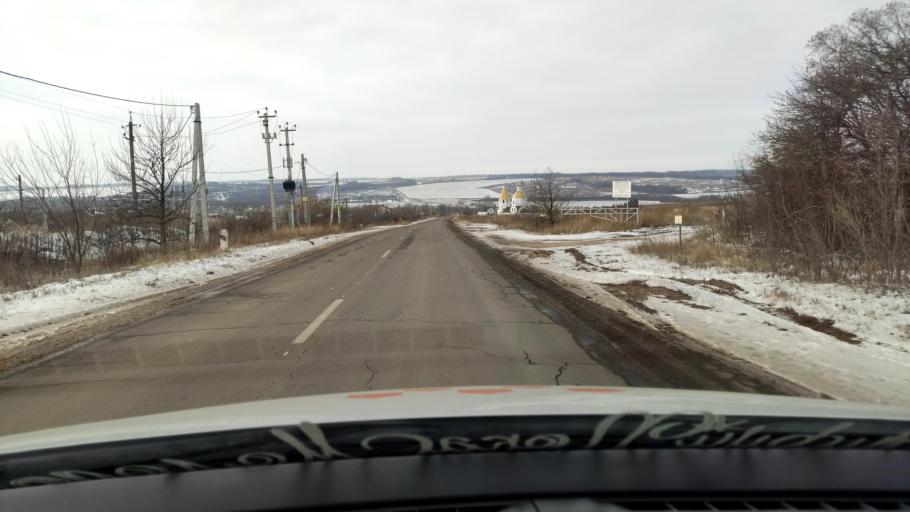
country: RU
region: Voronezj
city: Semiluki
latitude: 51.7491
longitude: 39.0388
